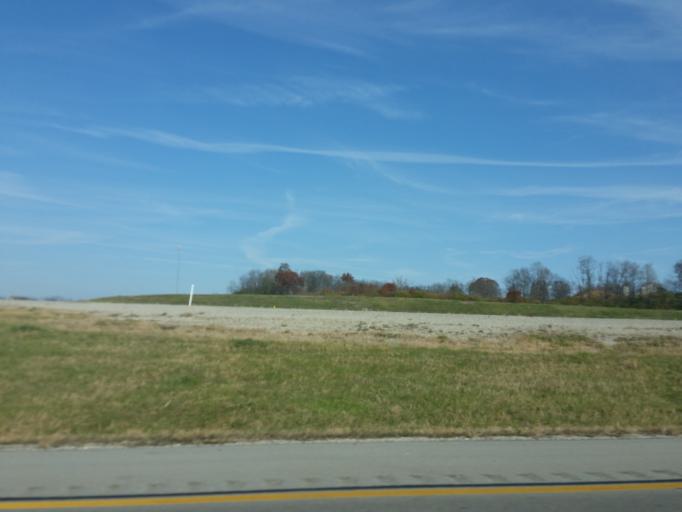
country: US
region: Kentucky
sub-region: Campbell County
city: Highland Heights
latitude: 39.0439
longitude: -84.4587
